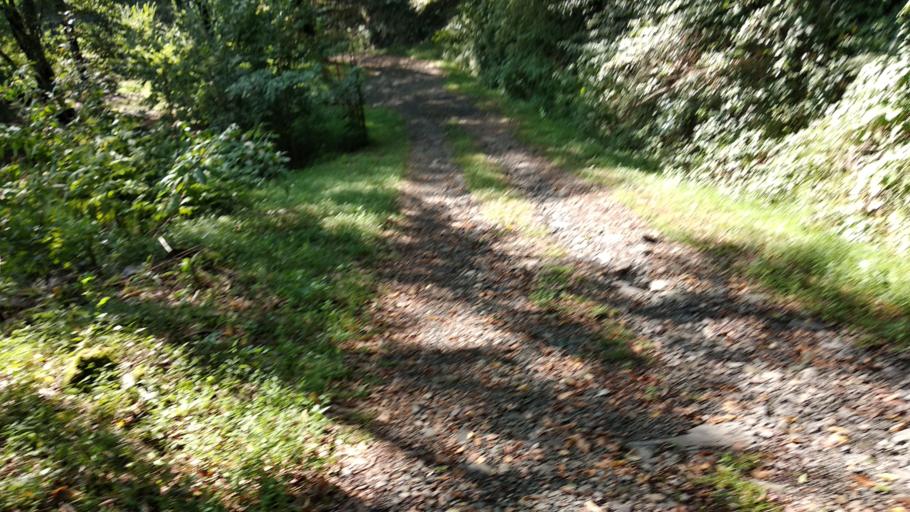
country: RU
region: Krasnodarskiy
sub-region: Sochi City
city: Sochi
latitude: 43.6357
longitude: 39.8220
